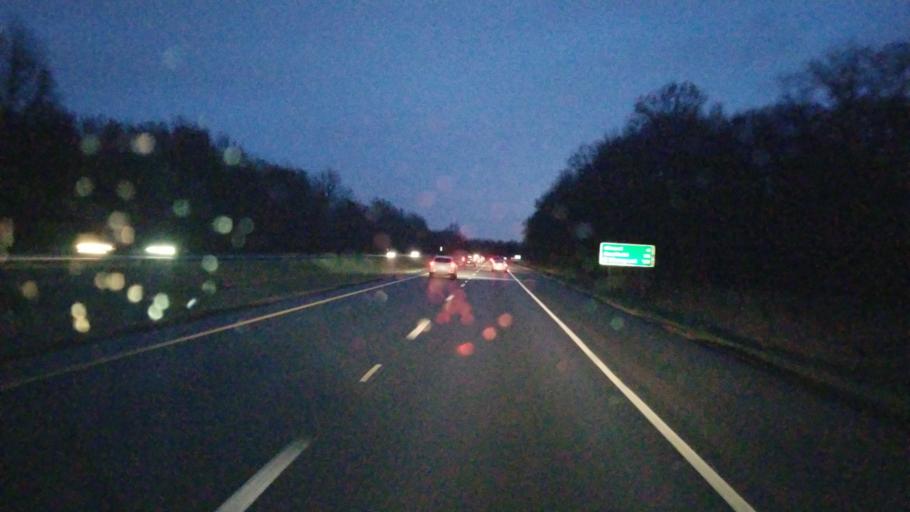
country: US
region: Ohio
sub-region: Trumbull County
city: Churchill
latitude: 41.1723
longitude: -80.6816
